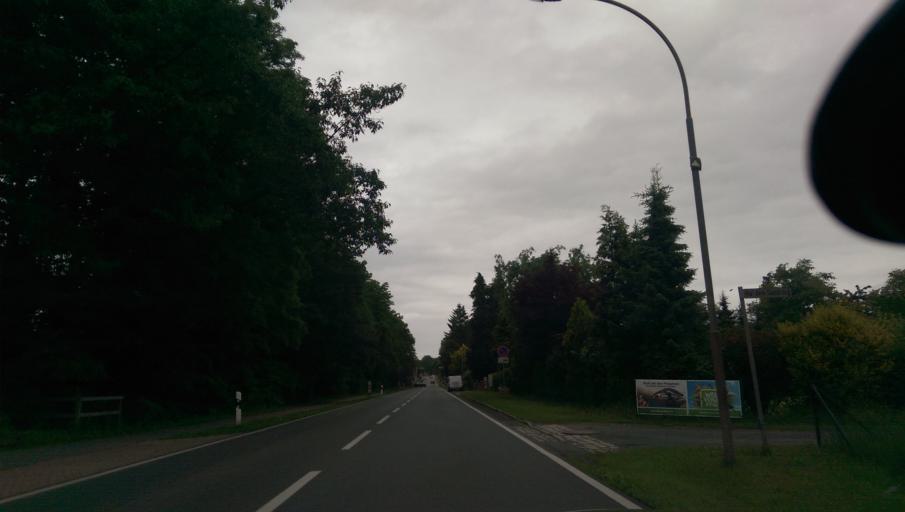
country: DE
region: Lower Saxony
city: Visselhovede
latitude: 52.9780
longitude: 9.5957
